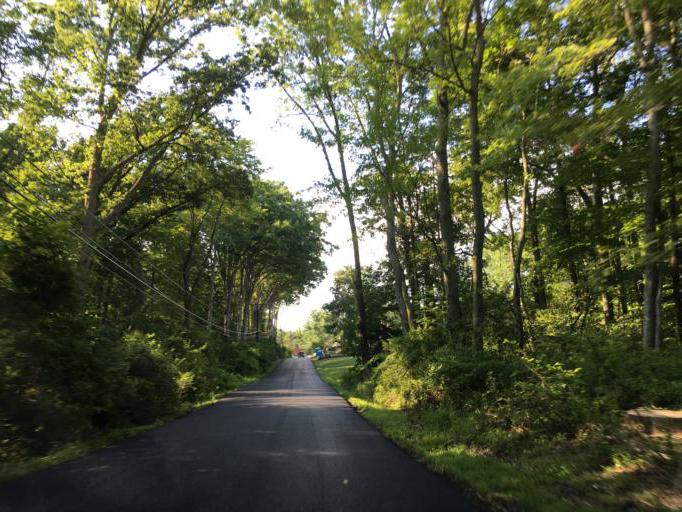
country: US
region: Maryland
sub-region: Baltimore County
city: Kingsville
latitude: 39.4640
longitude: -76.4392
